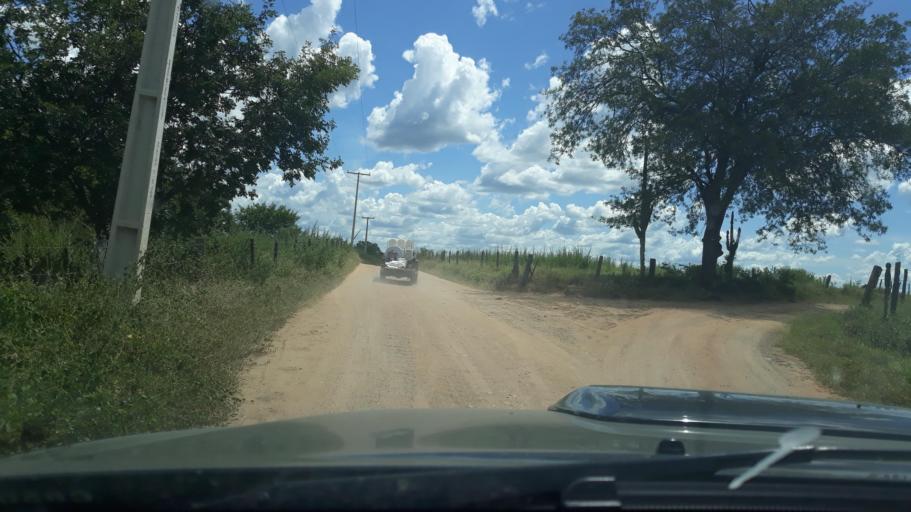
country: BR
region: Bahia
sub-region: Riacho De Santana
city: Riacho de Santana
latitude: -13.9050
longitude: -42.8992
